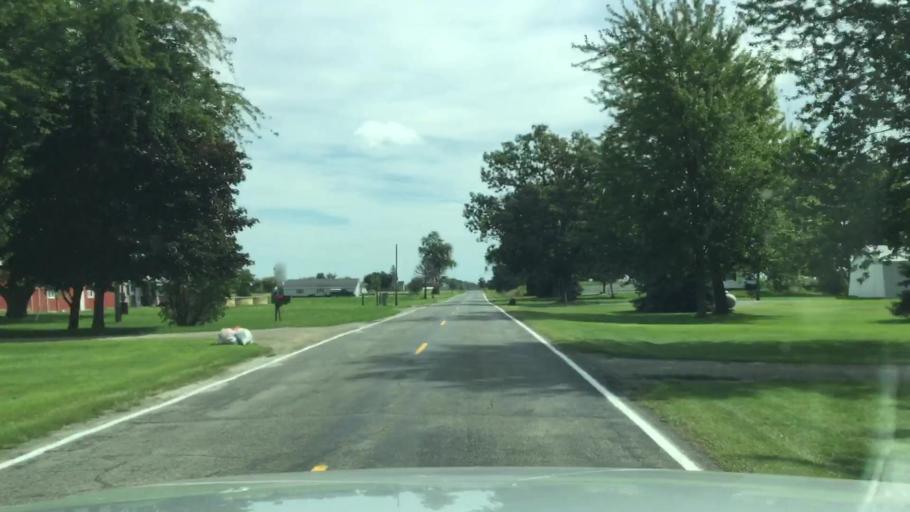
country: US
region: Michigan
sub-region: Genesee County
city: Montrose
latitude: 43.1466
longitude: -83.9966
